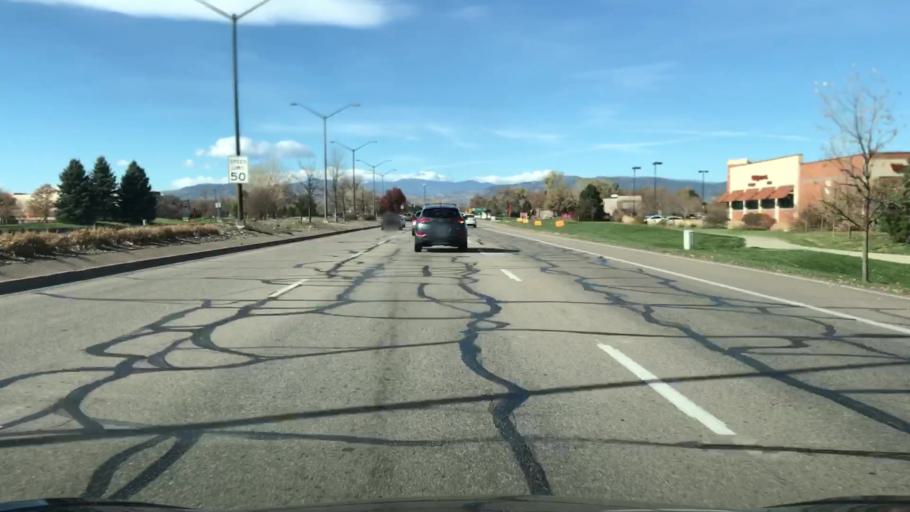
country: US
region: Colorado
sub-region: Larimer County
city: Fort Collins
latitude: 40.5234
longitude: -105.0341
